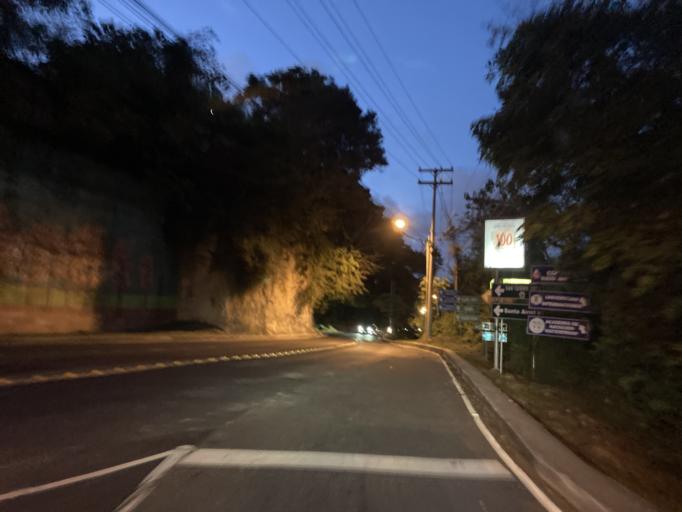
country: GT
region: Guatemala
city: Santa Catarina Pinula
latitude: 14.5988
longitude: -90.4664
